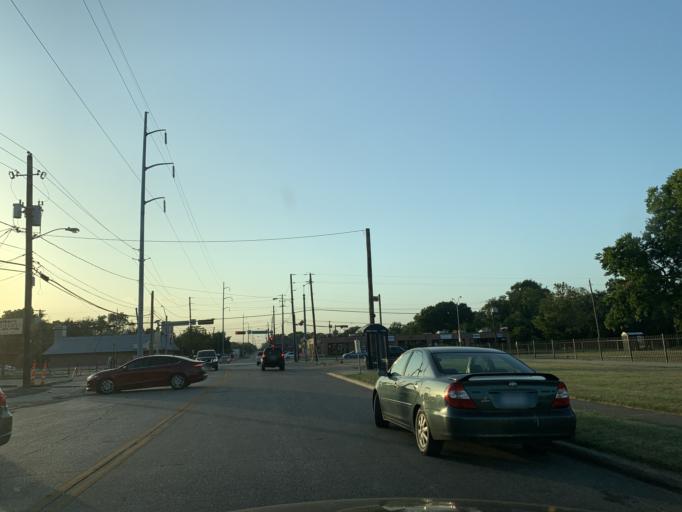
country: US
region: Texas
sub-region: Dallas County
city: Dallas
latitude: 32.7555
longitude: -96.7523
